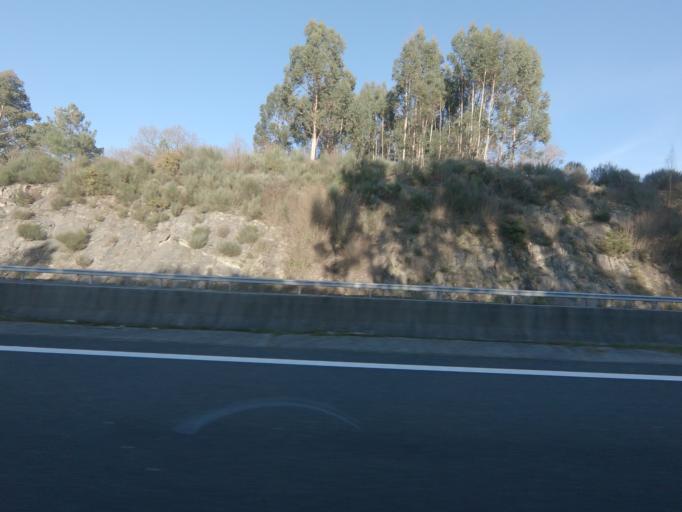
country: ES
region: Galicia
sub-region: Provincia de Ourense
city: Pinor
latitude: 42.4926
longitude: -8.0252
